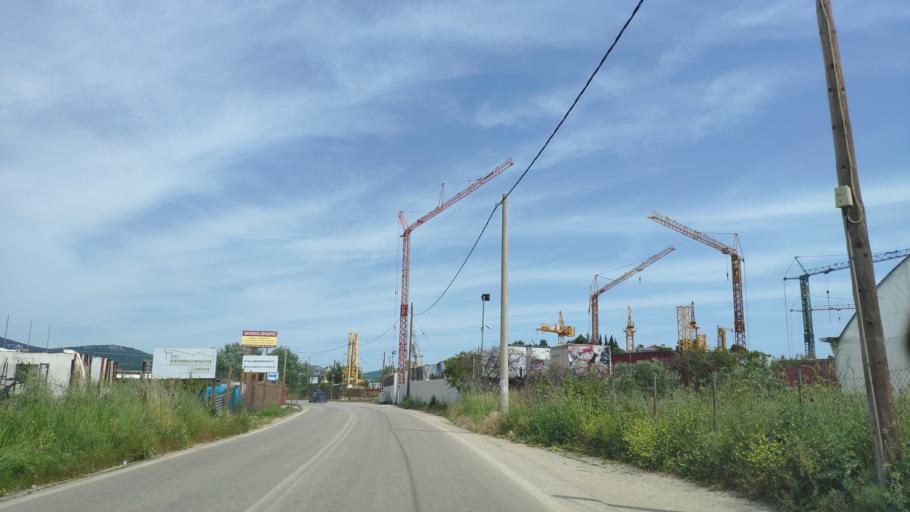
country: GR
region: Attica
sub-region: Nomarchia Anatolikis Attikis
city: Afidnes
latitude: 38.1823
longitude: 23.8565
